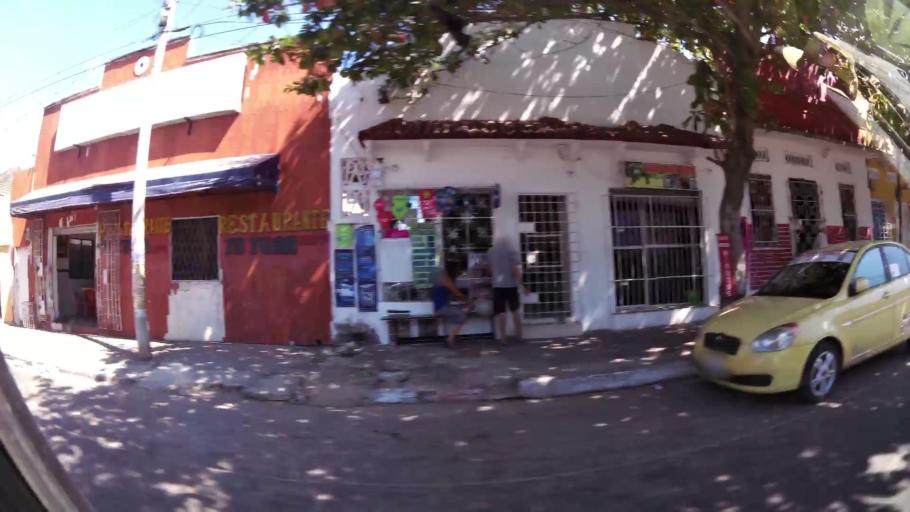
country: CO
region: Atlantico
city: Barranquilla
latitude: 10.9723
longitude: -74.7837
